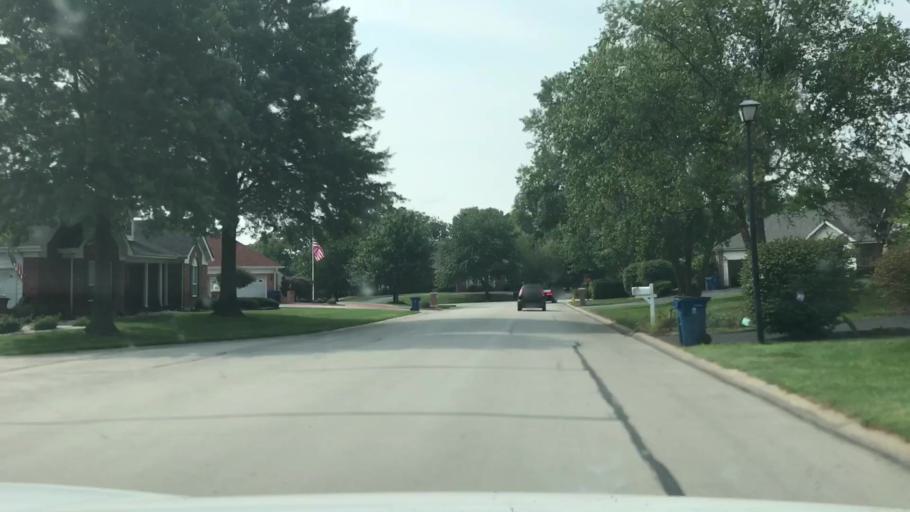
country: US
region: Missouri
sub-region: Saint Charles County
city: Cottleville
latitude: 38.7134
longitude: -90.6349
